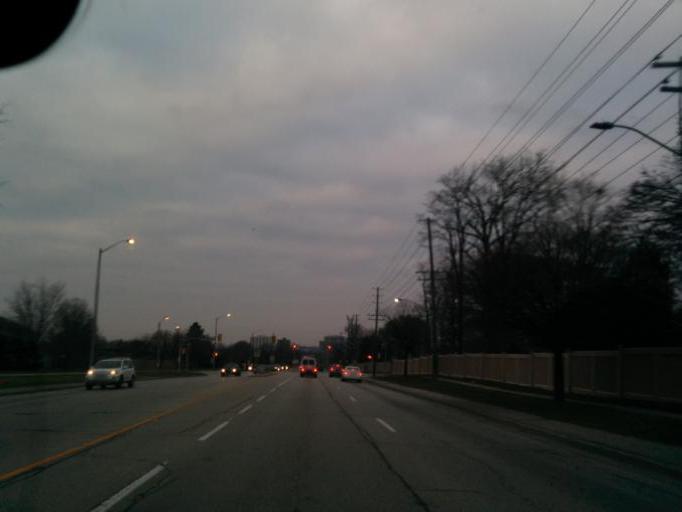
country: CA
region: Ontario
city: Etobicoke
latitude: 43.6276
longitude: -79.5969
